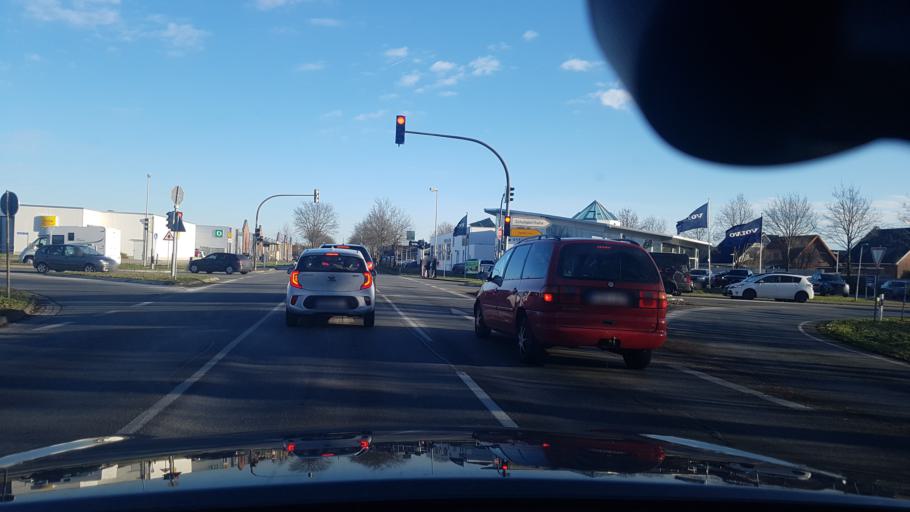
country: DE
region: Lower Saxony
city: Langen
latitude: 53.5804
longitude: 8.6279
